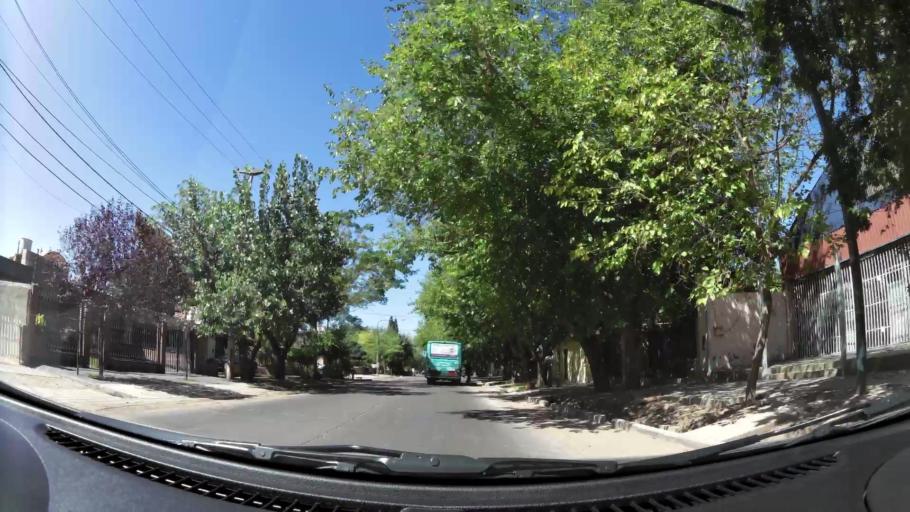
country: AR
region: Mendoza
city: Mendoza
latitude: -32.8858
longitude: -68.8063
